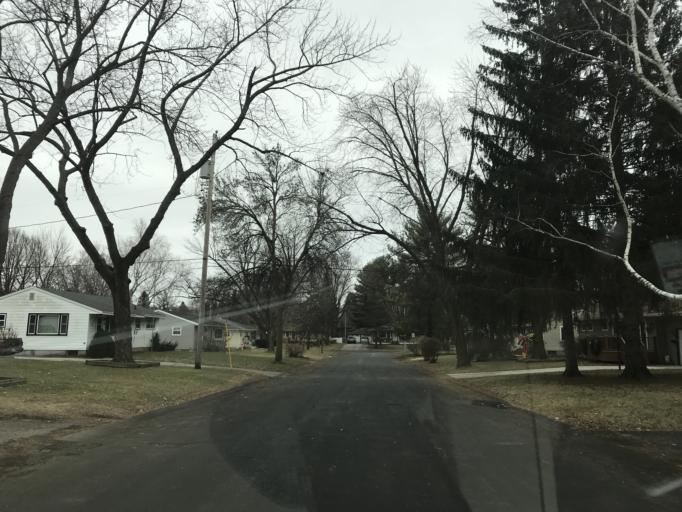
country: US
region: Wisconsin
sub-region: Dane County
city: Monona
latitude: 43.0603
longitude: -89.3210
